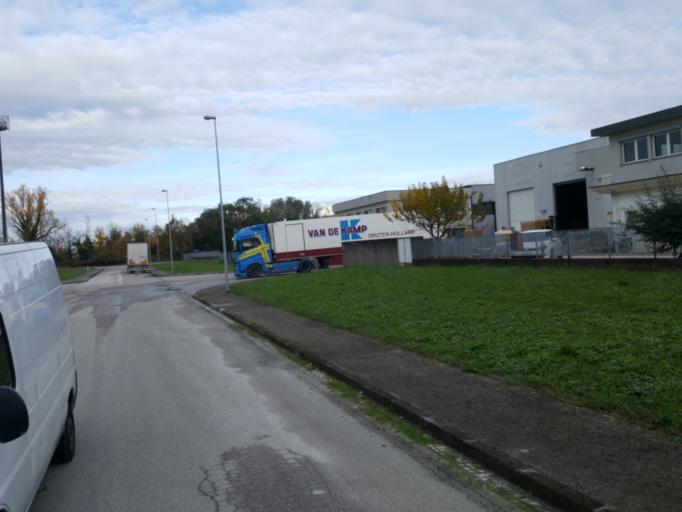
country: IT
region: Friuli Venezia Giulia
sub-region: Provincia di Udine
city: Manzano
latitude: 45.9880
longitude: 13.3635
